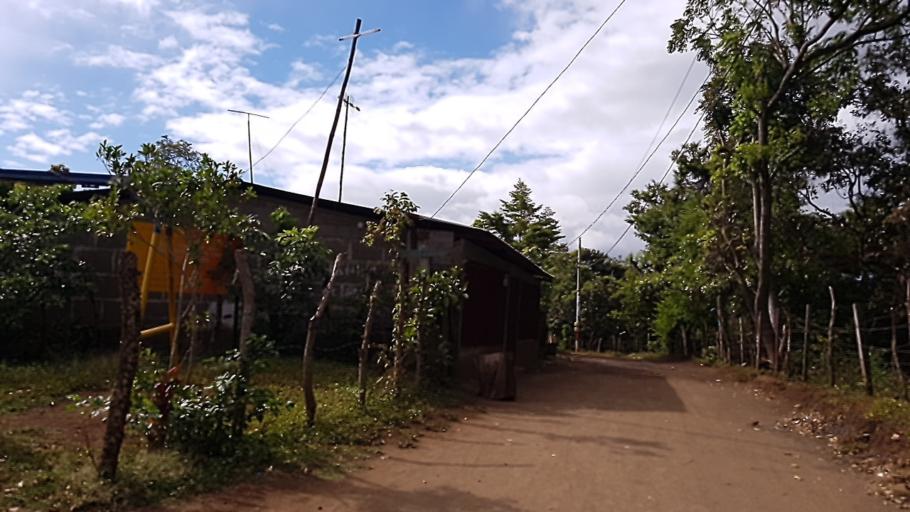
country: NI
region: Carazo
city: La Paz de Oriente
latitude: 11.8196
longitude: -86.1302
